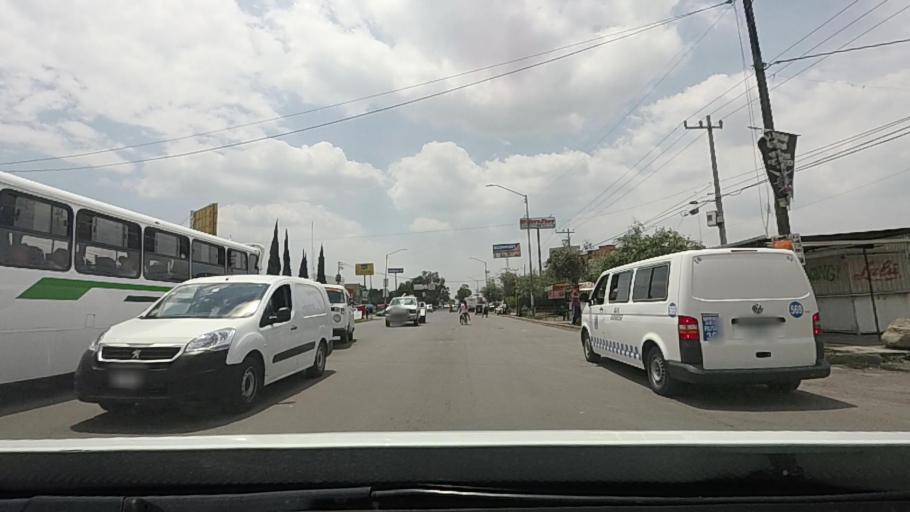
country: MX
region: Mexico
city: Chalco de Diaz Covarrubias
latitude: 19.2792
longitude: -98.9100
